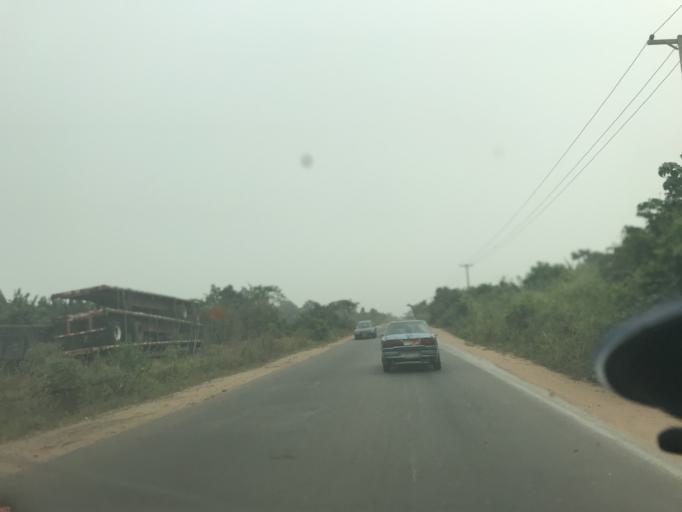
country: NG
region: Ogun
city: Itori
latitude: 6.8908
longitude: 3.1671
